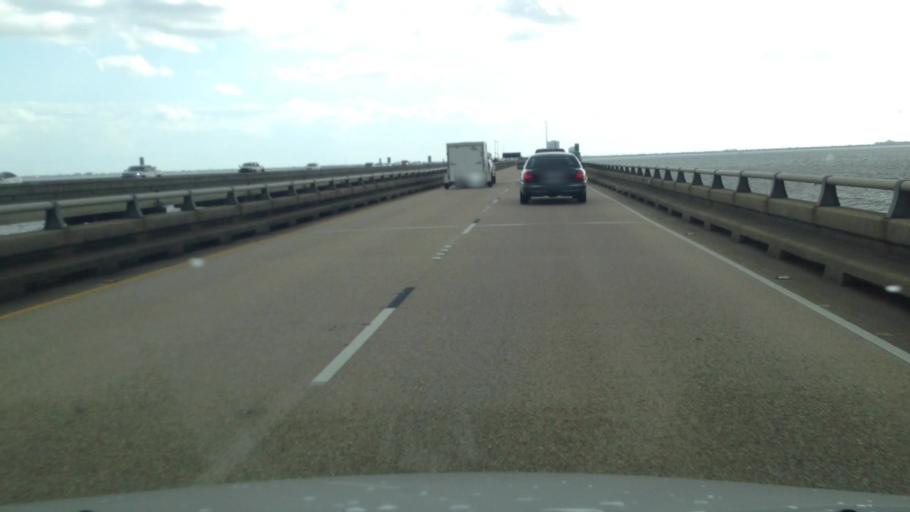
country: US
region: Louisiana
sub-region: Jefferson Parish
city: Metairie
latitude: 30.0753
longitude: -90.1447
